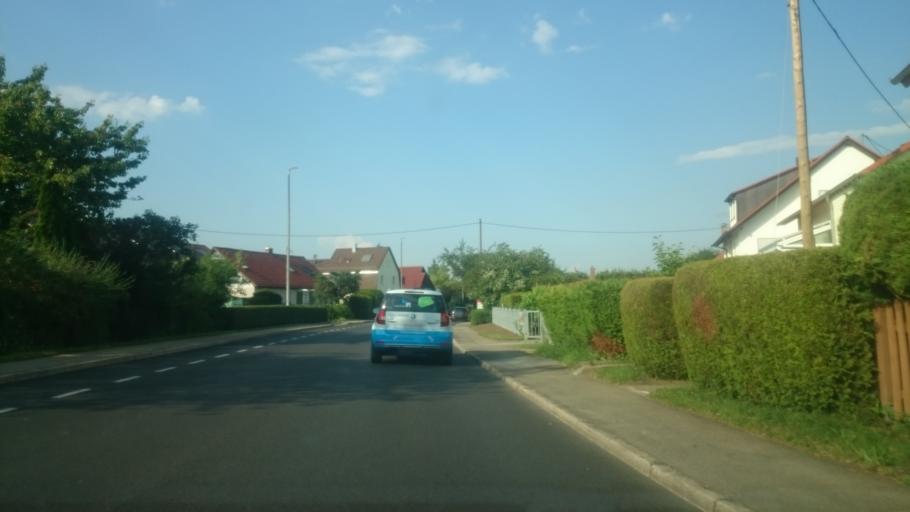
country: DE
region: Baden-Wuerttemberg
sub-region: Tuebingen Region
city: Wannweil
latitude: 48.4778
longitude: 9.1342
